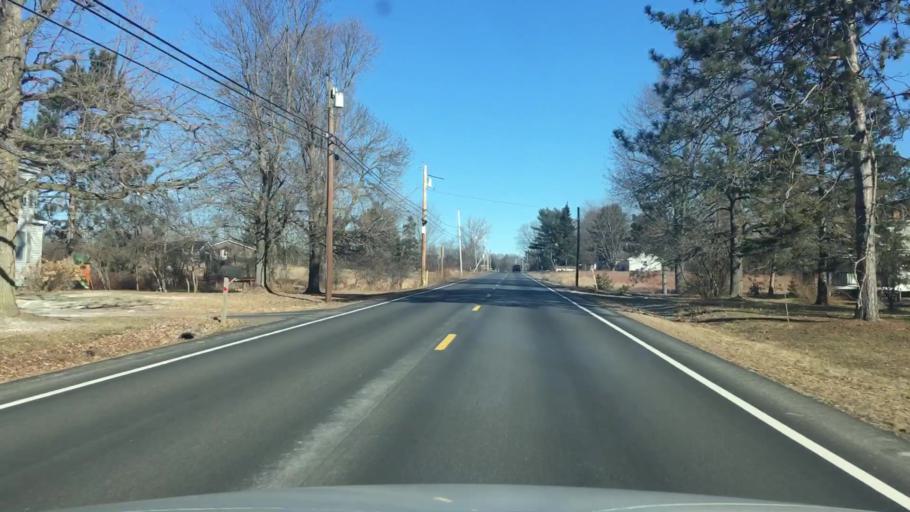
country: US
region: Maine
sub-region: Kennebec County
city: Benton
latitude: 44.5898
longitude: -69.5484
